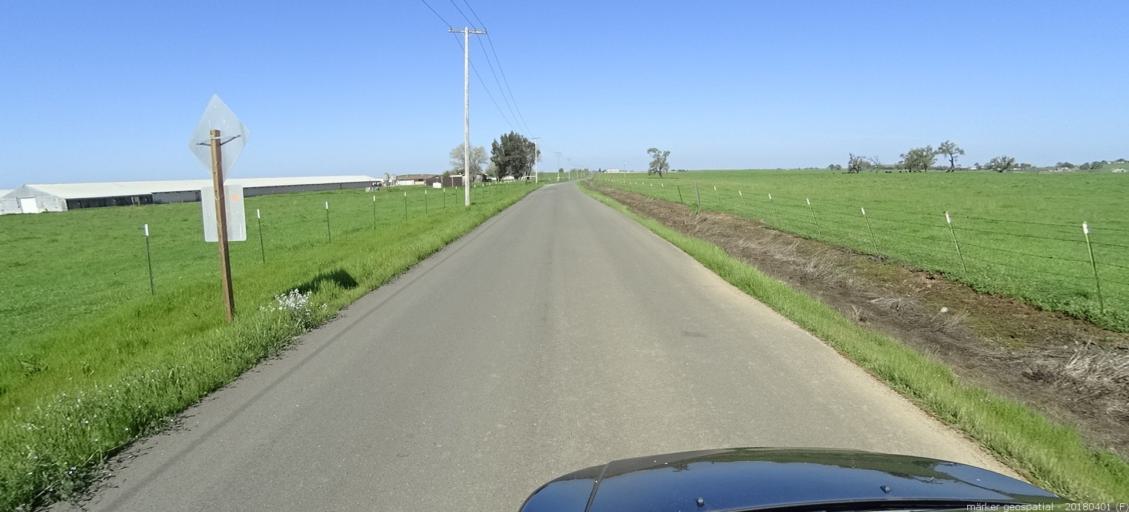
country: US
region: California
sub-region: Sacramento County
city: Rancho Murieta
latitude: 38.4672
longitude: -121.1585
